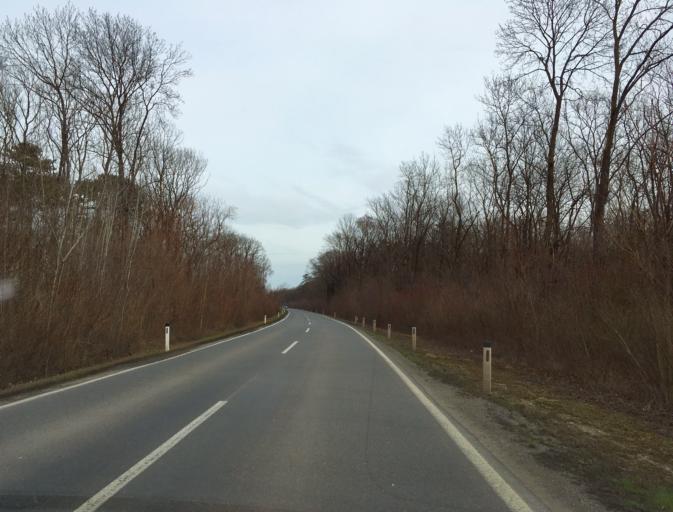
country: AT
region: Lower Austria
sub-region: Politischer Bezirk Ganserndorf
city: Leopoldsdorf im Marchfelde
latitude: 48.2264
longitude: 16.7001
